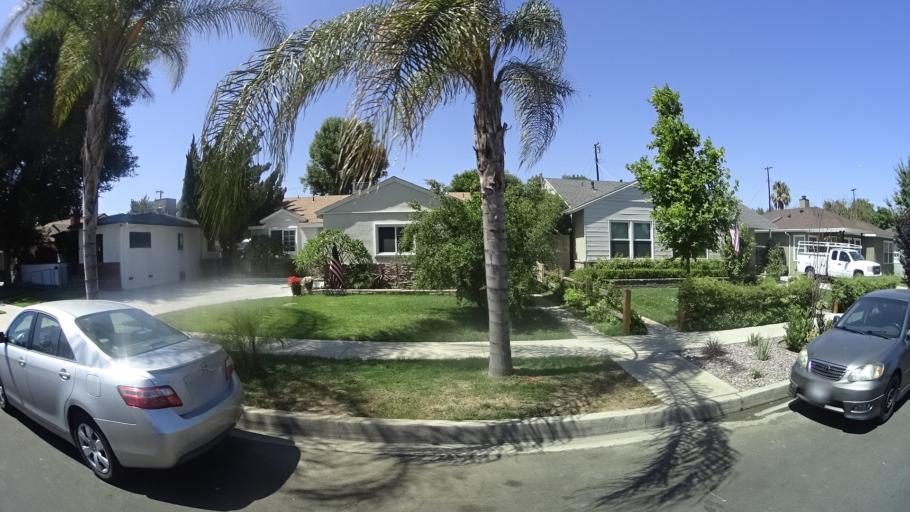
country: US
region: California
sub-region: Los Angeles County
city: Van Nuys
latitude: 34.1876
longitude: -118.4953
